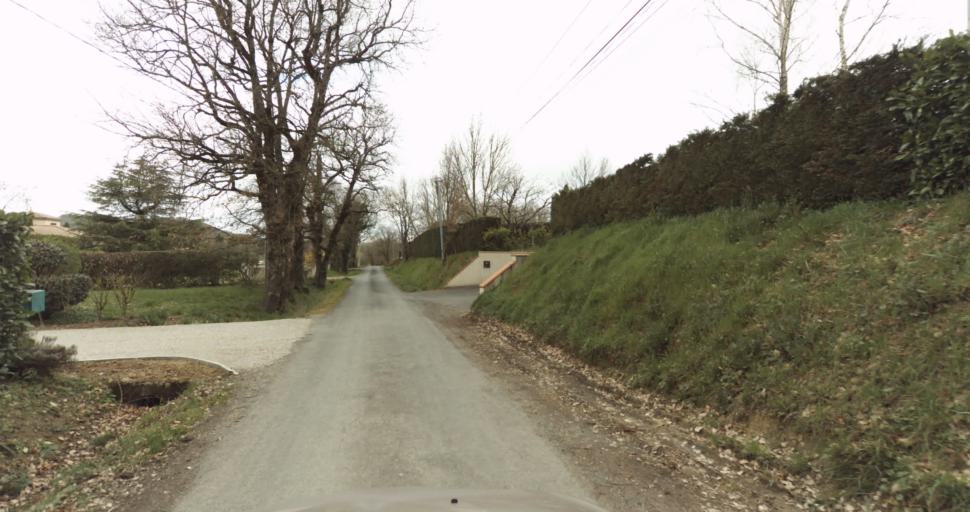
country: FR
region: Midi-Pyrenees
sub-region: Departement du Tarn
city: Puygouzon
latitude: 43.8869
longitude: 2.1618
